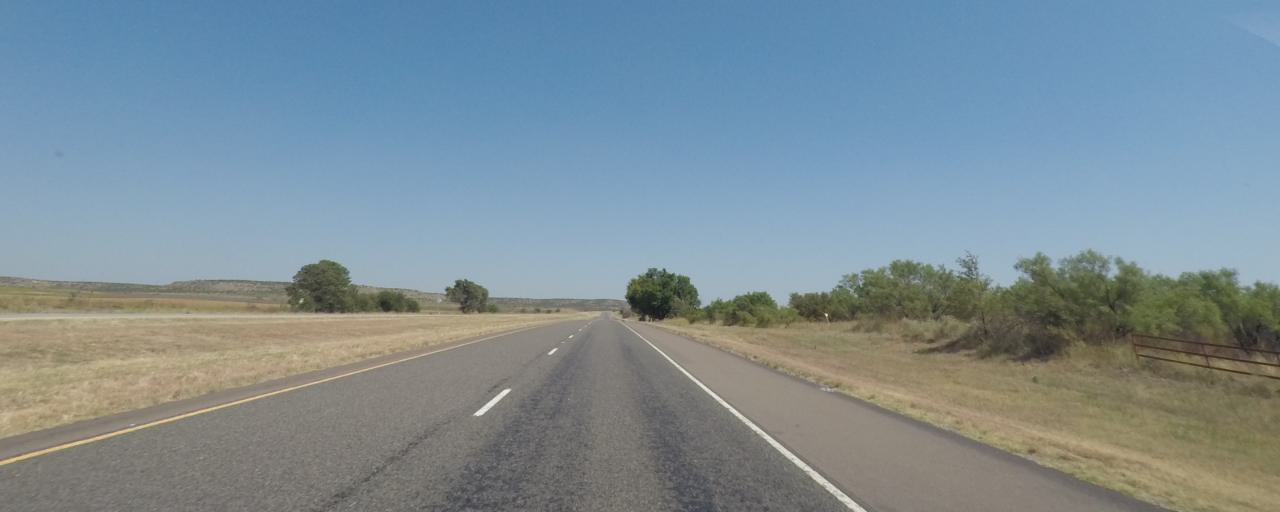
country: US
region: Texas
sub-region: Dickens County
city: Dickens
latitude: 33.6367
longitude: -100.8985
